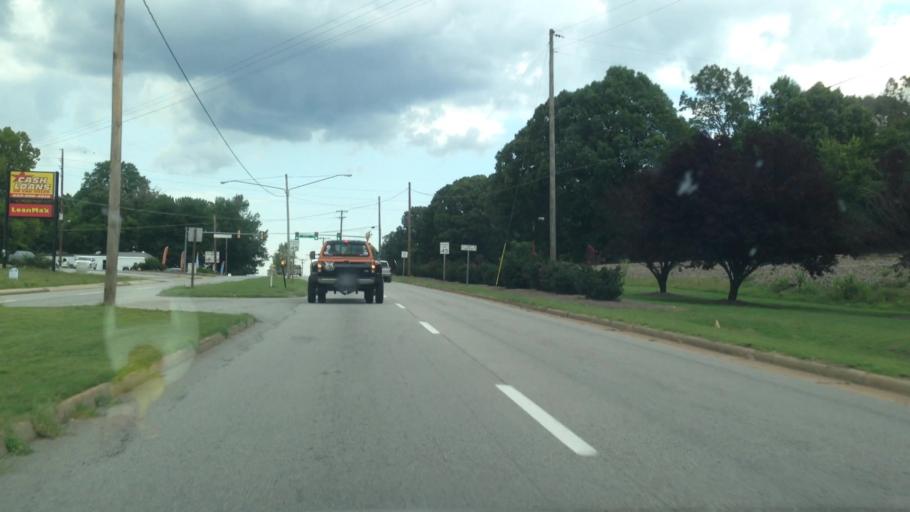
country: US
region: Virginia
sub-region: City of Danville
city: Danville
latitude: 36.5463
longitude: -79.4619
